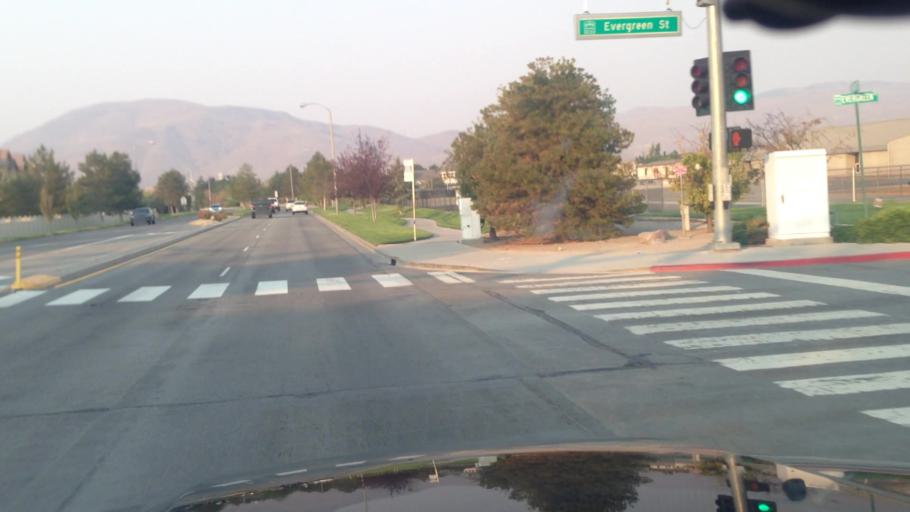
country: US
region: Nevada
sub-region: Washoe County
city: Sparks
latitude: 39.4417
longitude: -119.7492
